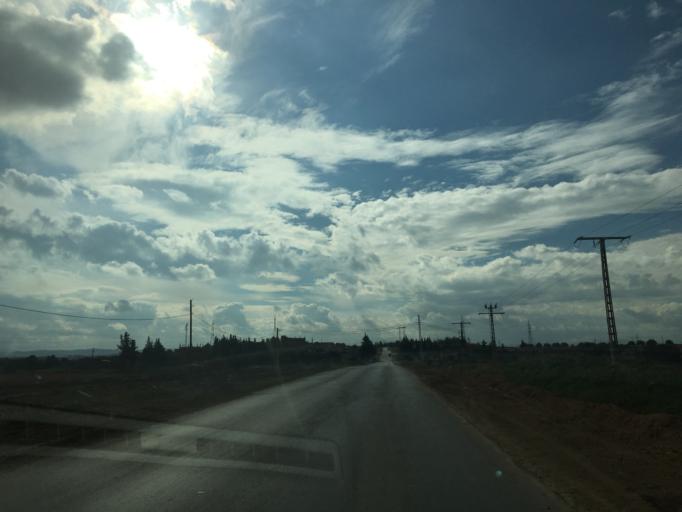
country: DZ
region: Bouira
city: Bouira
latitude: 36.3163
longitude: 3.8644
